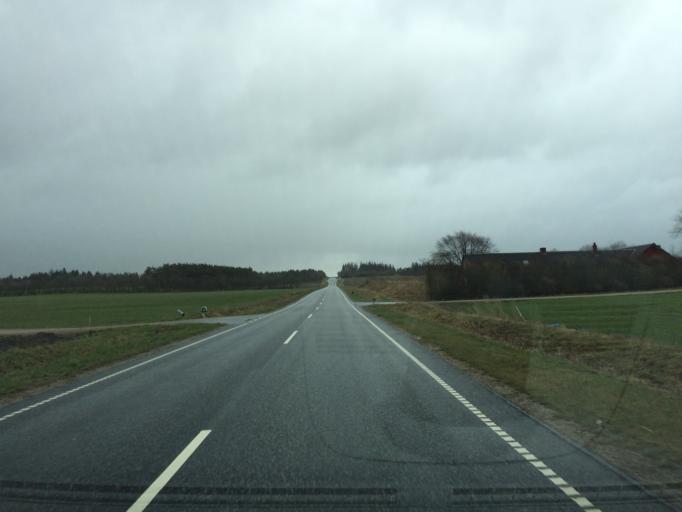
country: DK
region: Central Jutland
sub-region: Ringkobing-Skjern Kommune
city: Videbaek
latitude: 56.1860
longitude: 8.6322
